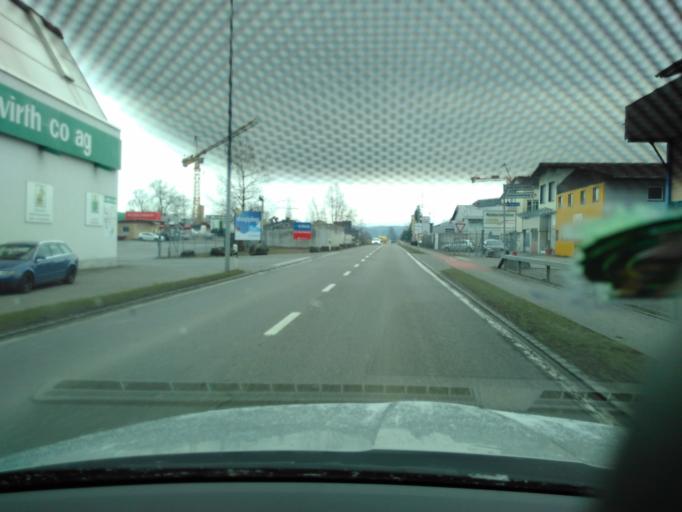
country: CH
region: Lucerne
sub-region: Lucerne-Land District
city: Buchrain
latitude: 47.1078
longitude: 8.3435
